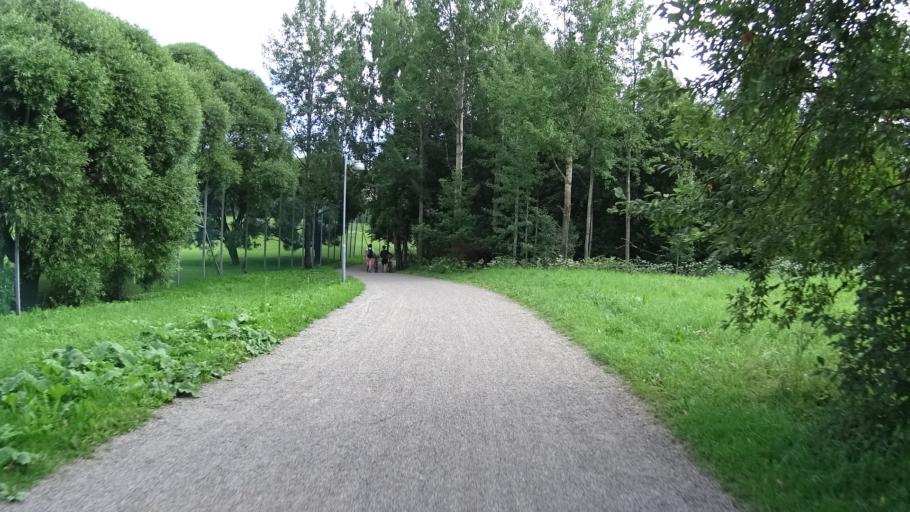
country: FI
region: Uusimaa
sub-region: Helsinki
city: Teekkarikylae
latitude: 60.2103
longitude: 24.8614
